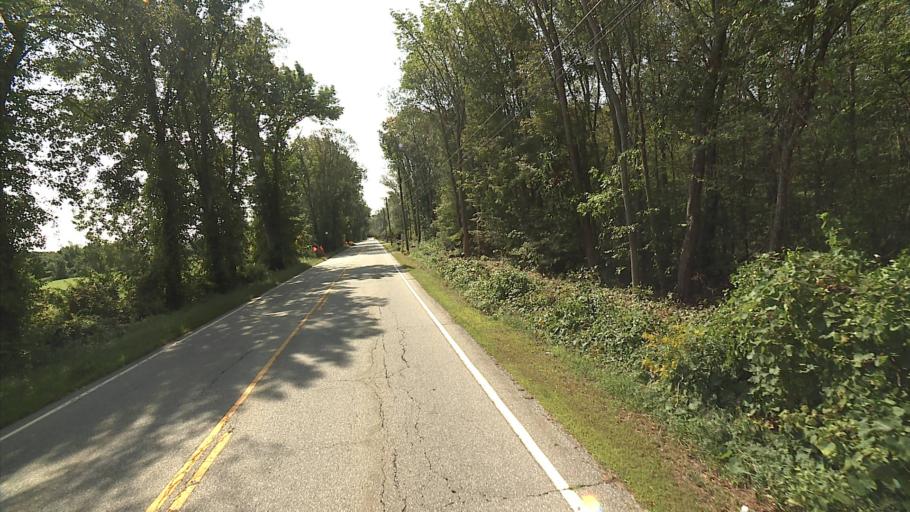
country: US
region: Connecticut
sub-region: Windham County
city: East Brooklyn
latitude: 41.8237
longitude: -71.9585
